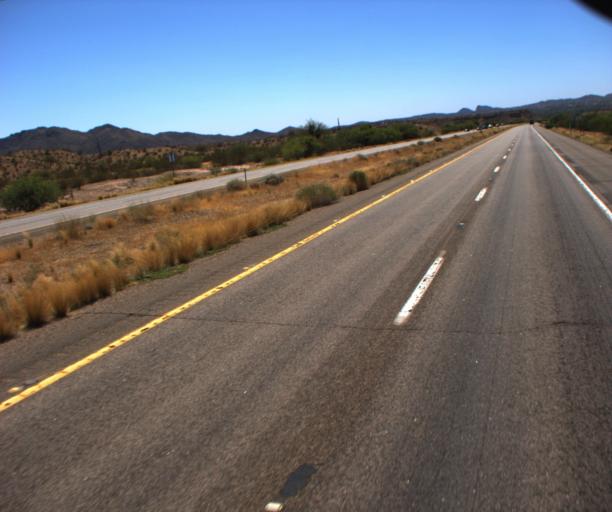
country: US
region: Arizona
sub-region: Maricopa County
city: Fountain Hills
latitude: 33.5812
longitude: -111.6399
